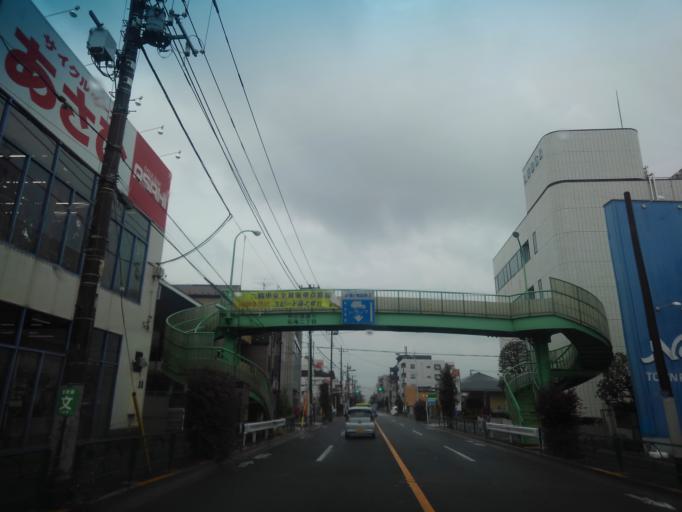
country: JP
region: Tokyo
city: Musashino
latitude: 35.6974
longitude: 139.5927
